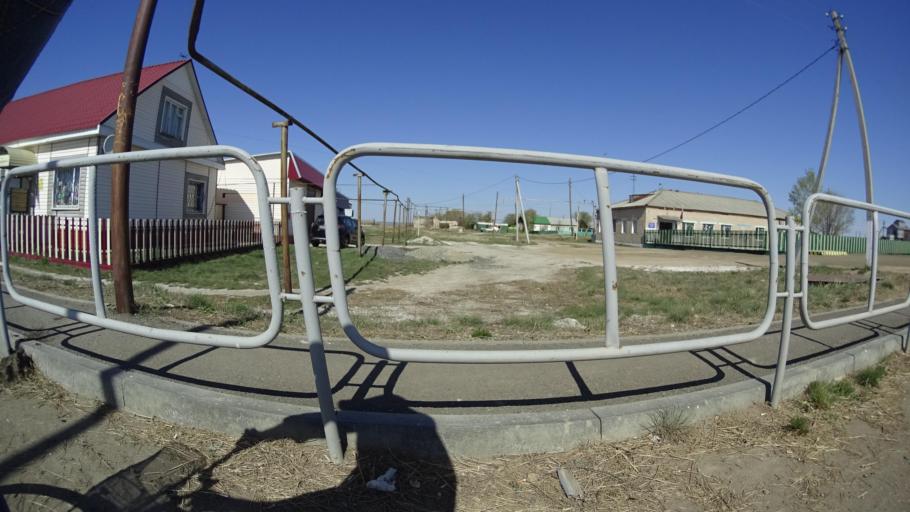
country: RU
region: Chelyabinsk
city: Chesma
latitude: 53.7958
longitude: 61.0329
